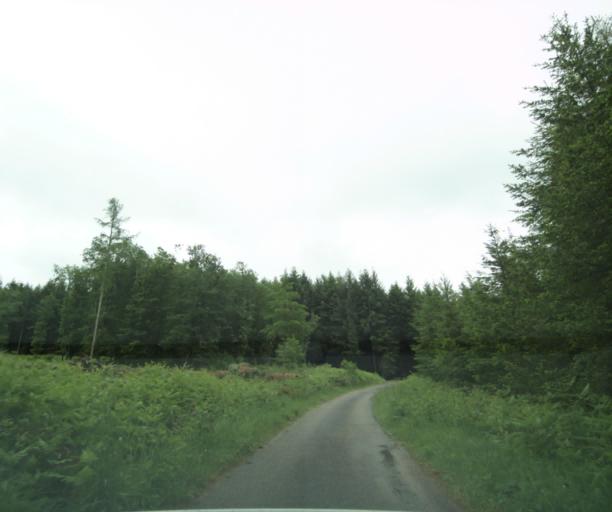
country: FR
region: Bourgogne
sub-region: Departement de Saone-et-Loire
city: Matour
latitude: 46.4499
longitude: 4.4655
